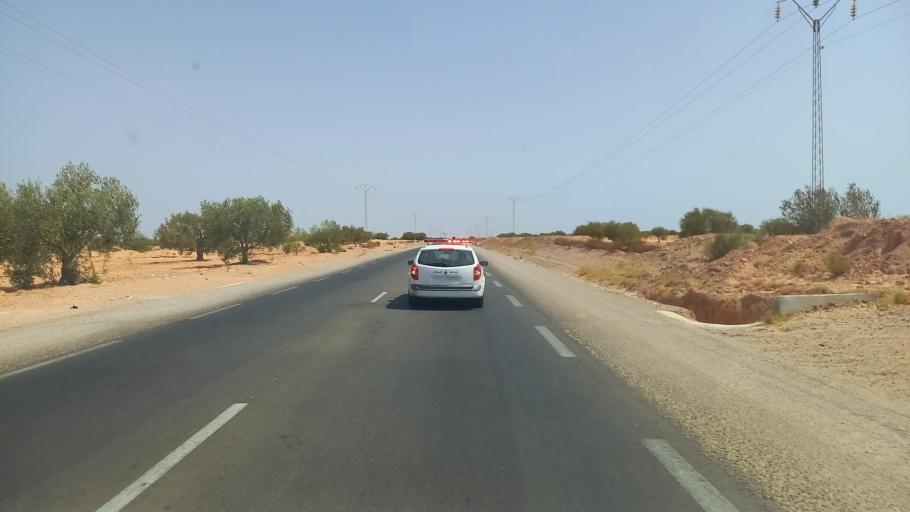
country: TN
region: Madanin
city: Zarzis
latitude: 33.4203
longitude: 10.8779
